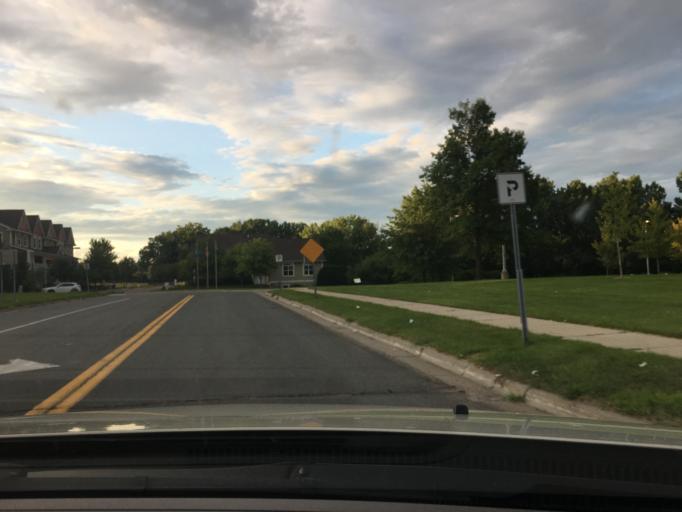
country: US
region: Minnesota
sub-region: Dakota County
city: West Saint Paul
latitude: 44.8982
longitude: -93.0784
